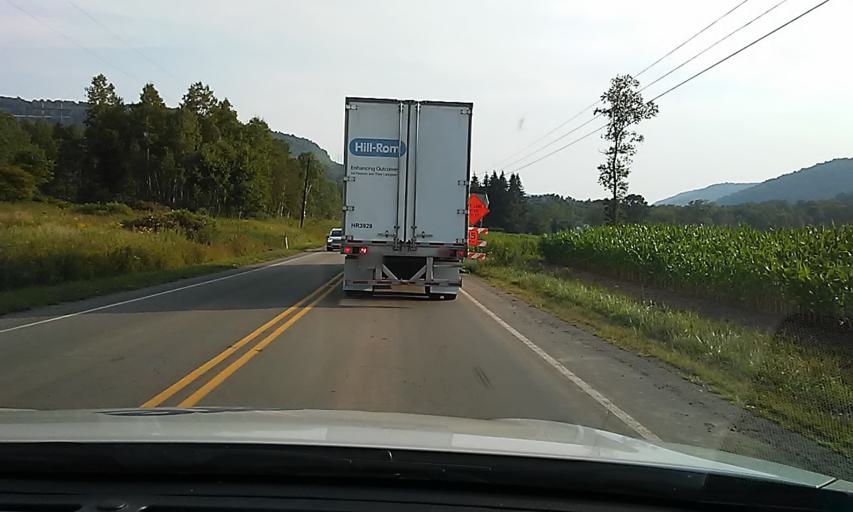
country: US
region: Pennsylvania
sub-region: McKean County
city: Smethport
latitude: 41.7535
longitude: -78.5247
